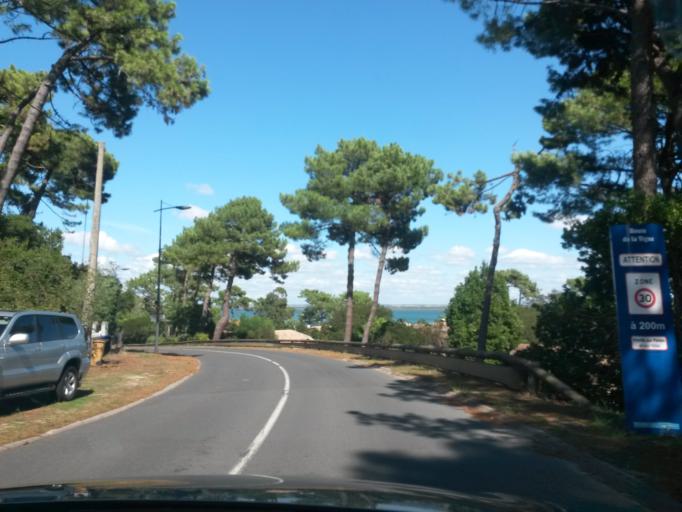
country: FR
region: Aquitaine
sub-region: Departement de la Gironde
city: Arcachon
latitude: 44.6698
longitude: -1.2415
